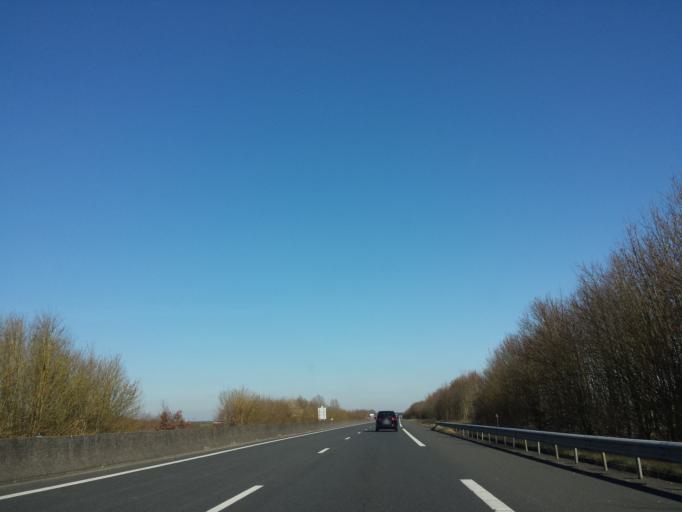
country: FR
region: Picardie
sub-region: Departement de l'Oise
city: Tille
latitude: 49.4738
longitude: 2.1630
